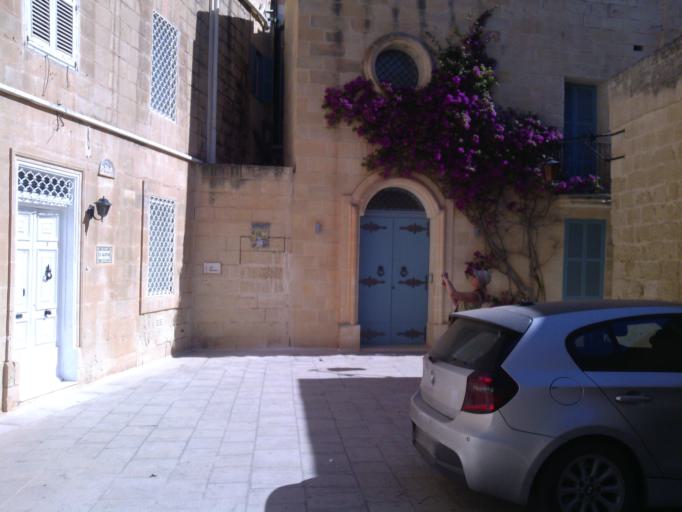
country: MT
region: L-Imdina
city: Imdina
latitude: 35.8874
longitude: 14.4024
